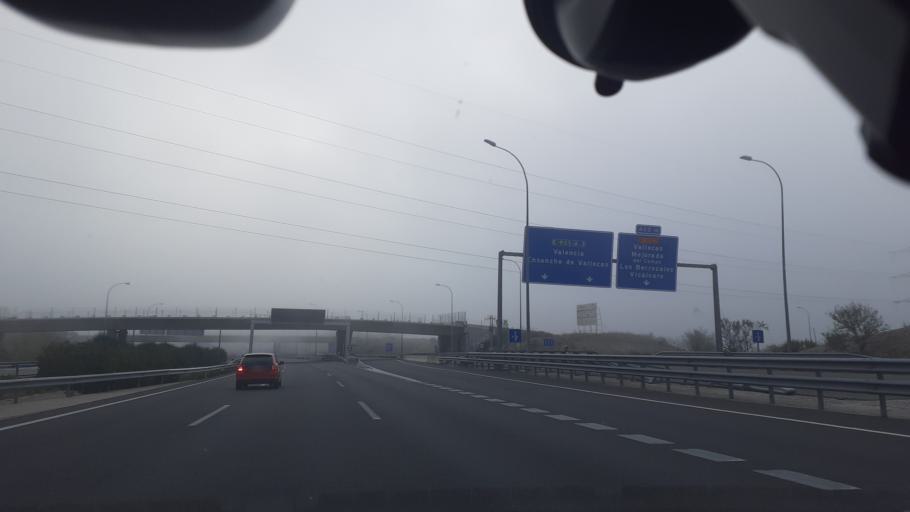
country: ES
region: Madrid
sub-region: Provincia de Madrid
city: Vicalvaro
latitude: 40.3894
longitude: -3.5825
